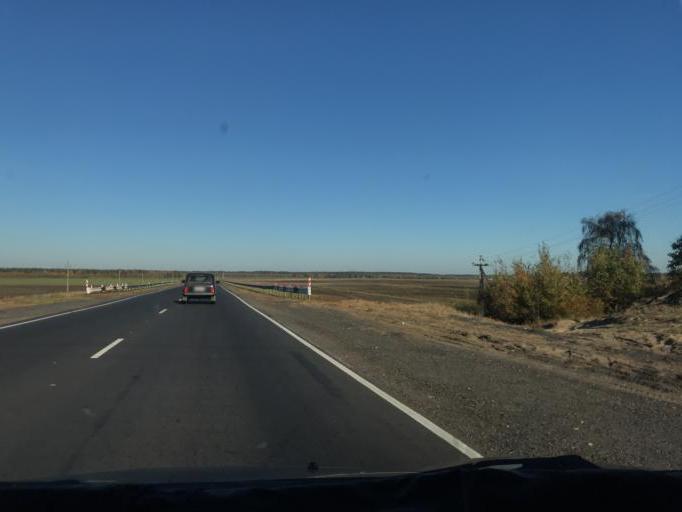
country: BY
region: Gomel
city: Mazyr
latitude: 52.0341
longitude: 29.3402
